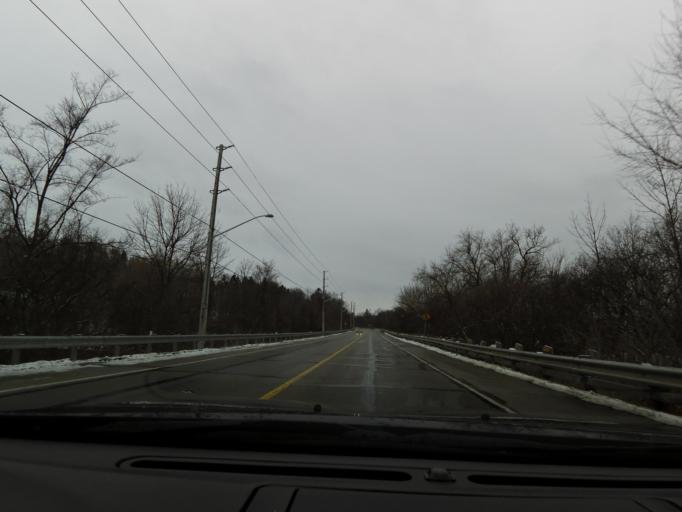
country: CA
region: Ontario
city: Ancaster
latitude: 43.2357
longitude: -79.9717
